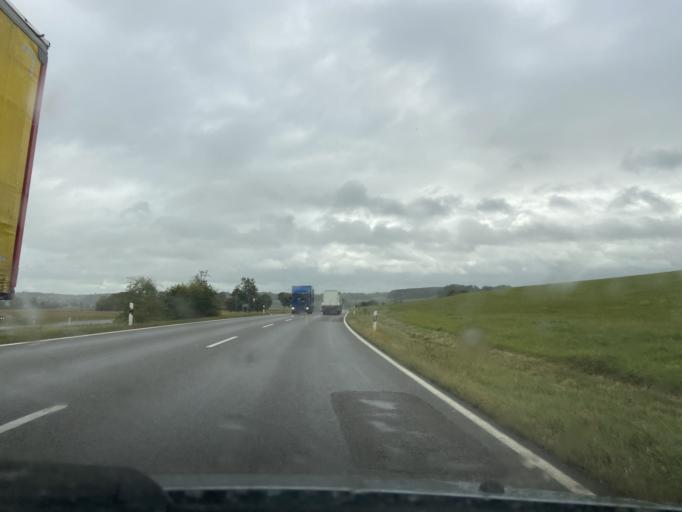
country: DE
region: Baden-Wuerttemberg
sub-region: Tuebingen Region
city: Messkirch
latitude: 48.0041
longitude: 9.1610
